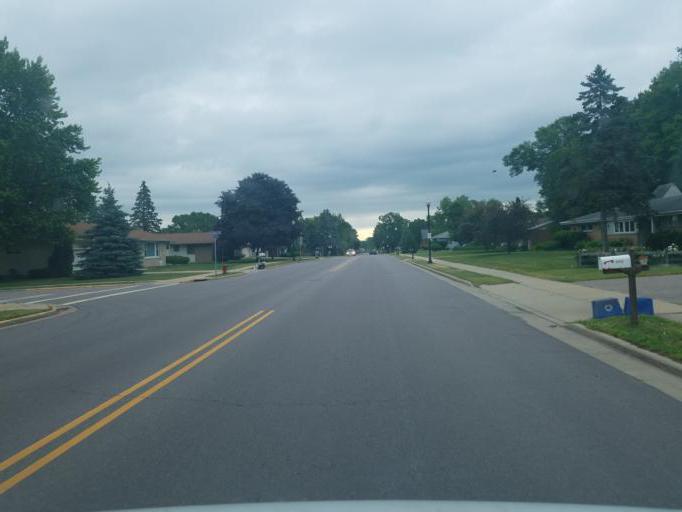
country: US
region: Wisconsin
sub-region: Juneau County
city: Mauston
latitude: 43.7891
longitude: -90.0821
